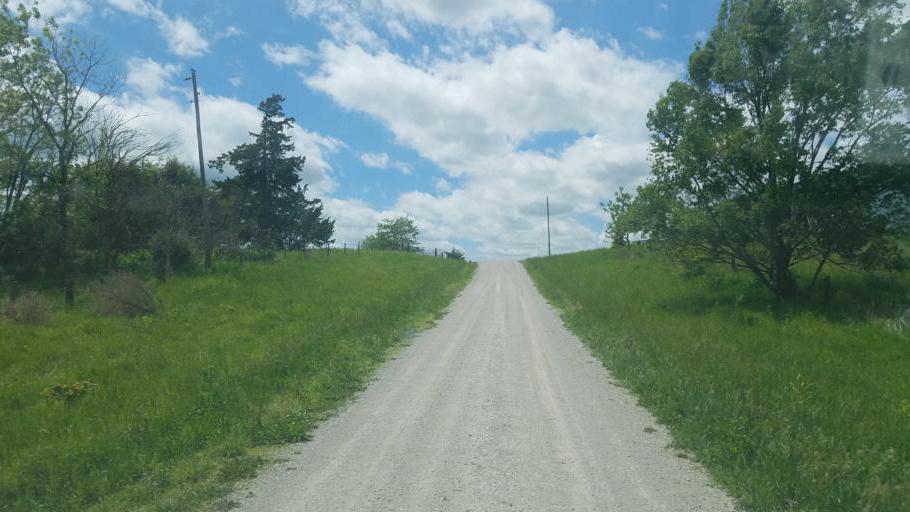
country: US
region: Iowa
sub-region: Decatur County
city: Lamoni
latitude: 40.5077
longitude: -94.0196
